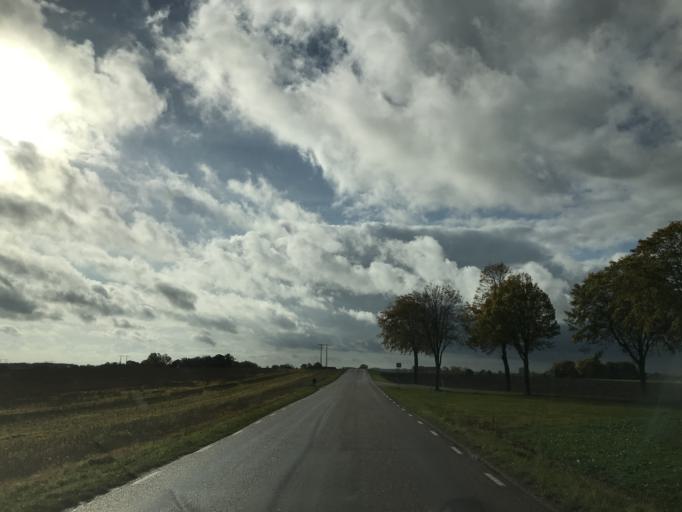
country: SE
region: Skane
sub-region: Svalovs Kommun
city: Svaloev
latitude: 55.8786
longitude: 13.1210
